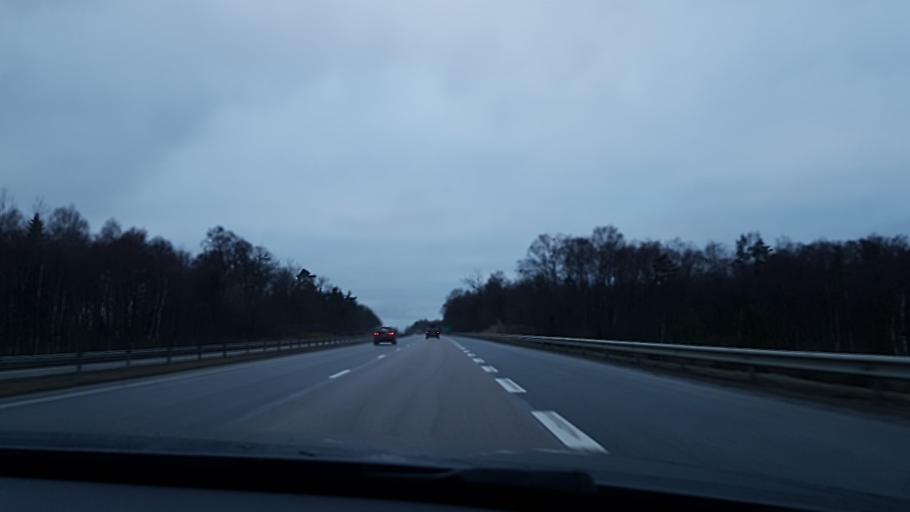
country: SE
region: Skane
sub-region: Klippans Kommun
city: Klippan
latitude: 56.2062
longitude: 13.0989
